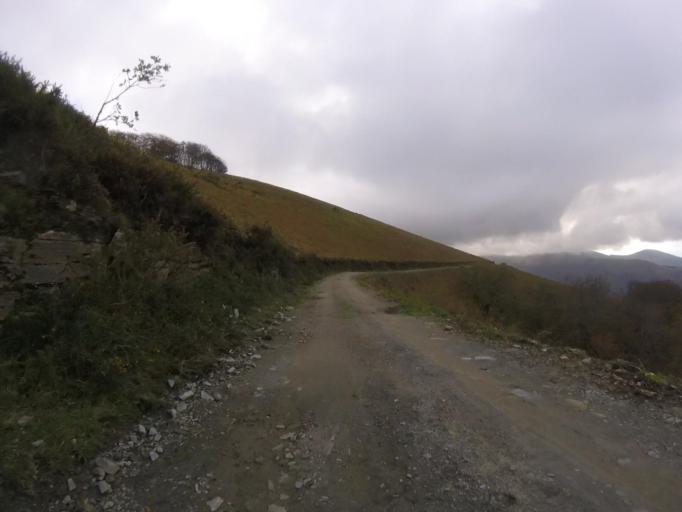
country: ES
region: Navarre
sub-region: Provincia de Navarra
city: Goizueta
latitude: 43.1981
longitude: -1.8239
